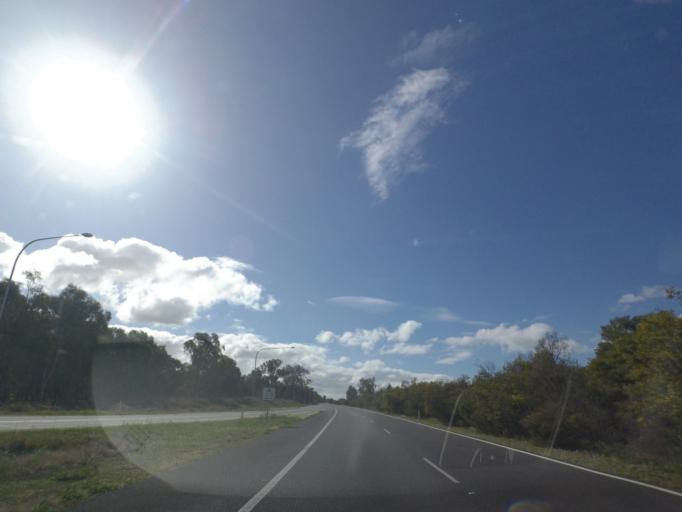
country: AU
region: New South Wales
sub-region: Albury Municipality
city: Lavington
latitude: -36.0370
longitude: 146.9747
